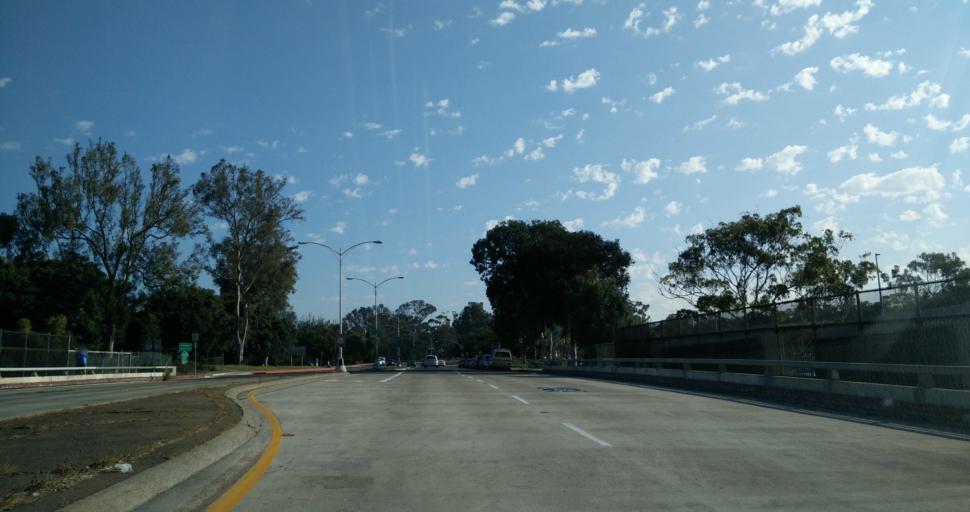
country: US
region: California
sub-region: San Diego County
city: San Diego
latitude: 32.7239
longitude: -117.1513
